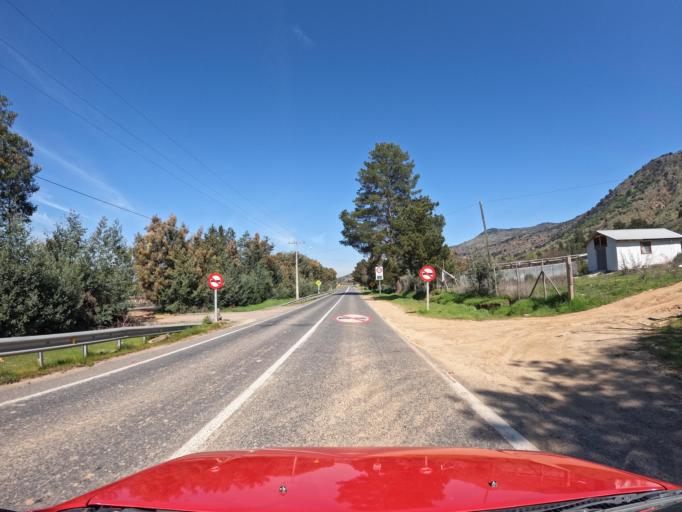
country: CL
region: Maule
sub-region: Provincia de Curico
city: Rauco
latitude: -35.0603
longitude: -71.6176
